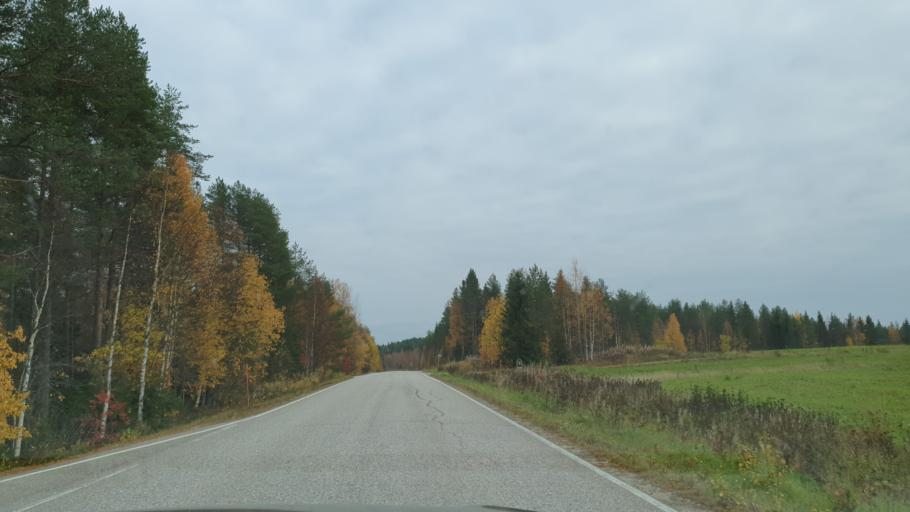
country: FI
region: Kainuu
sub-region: Kajaani
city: Ristijaervi
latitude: 64.4568
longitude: 28.3296
